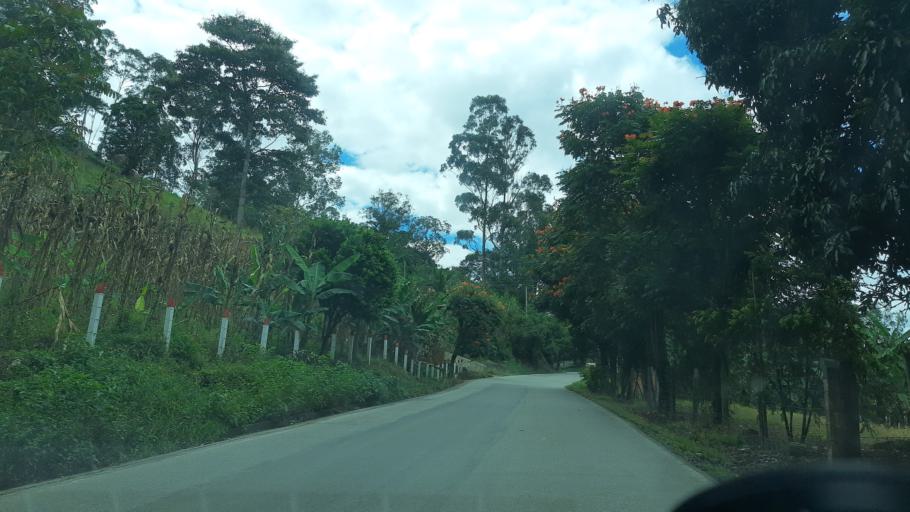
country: CO
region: Boyaca
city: Garagoa
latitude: 5.0617
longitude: -73.3832
